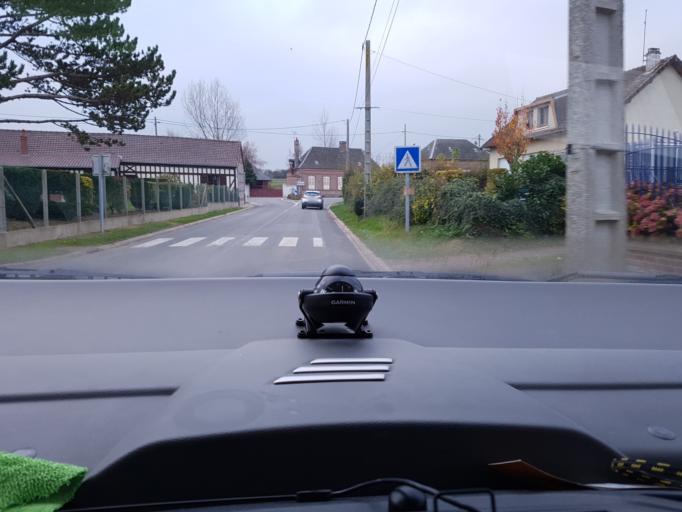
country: FR
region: Picardie
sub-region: Departement de la Somme
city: Cayeux-sur-Mer
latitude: 50.1395
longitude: 1.5193
